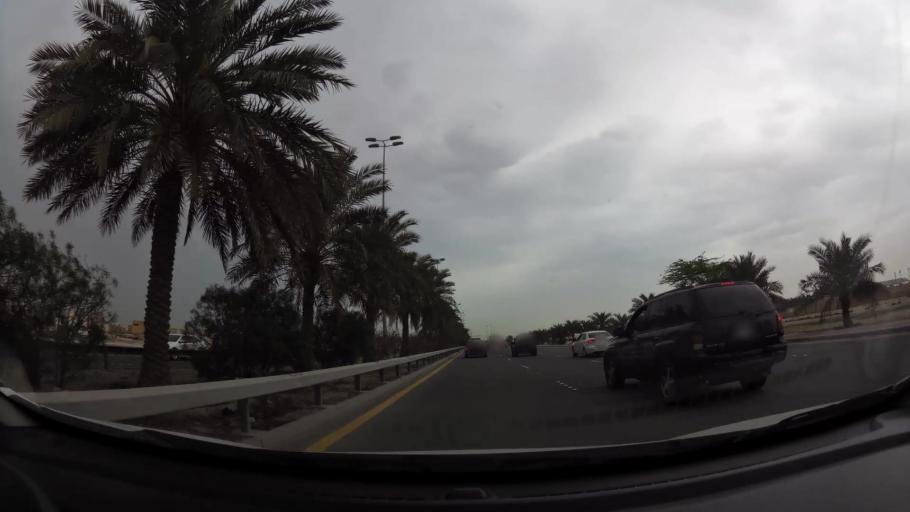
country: BH
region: Central Governorate
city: Dar Kulayb
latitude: 26.0577
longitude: 50.5053
